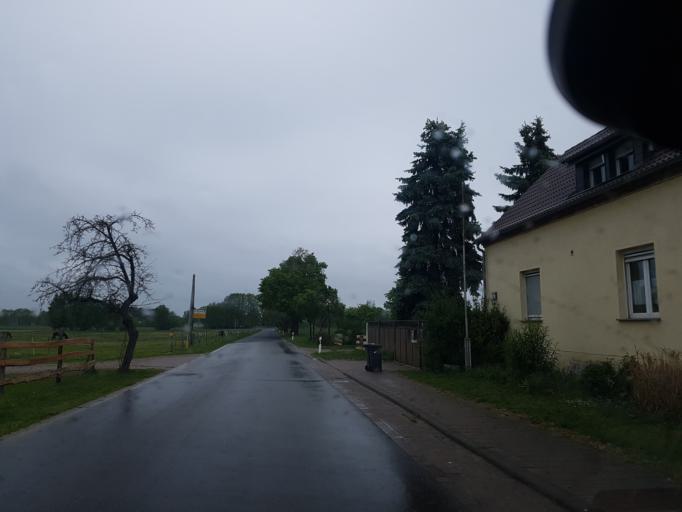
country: DE
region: Brandenburg
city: Spremberg
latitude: 51.6722
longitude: 14.4716
